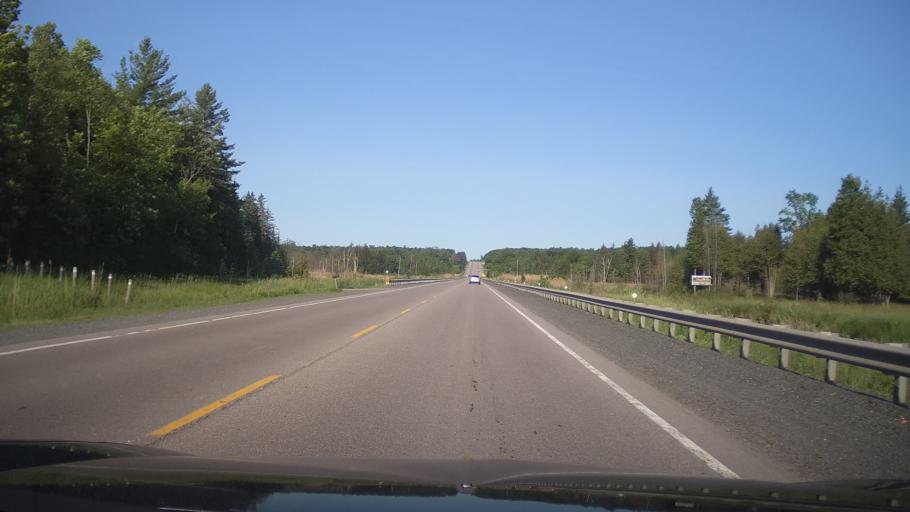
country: CA
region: Ontario
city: Quinte West
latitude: 44.4937
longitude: -77.6409
